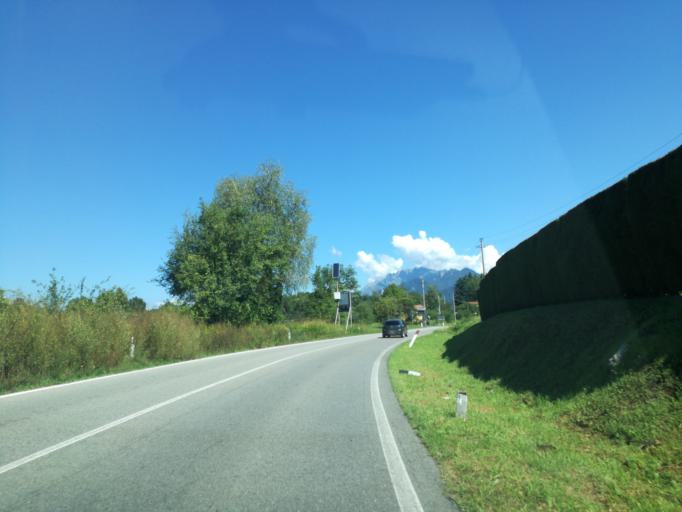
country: IT
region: Lombardy
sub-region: Provincia di Lecco
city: Arlate
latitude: 45.7297
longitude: 9.4410
